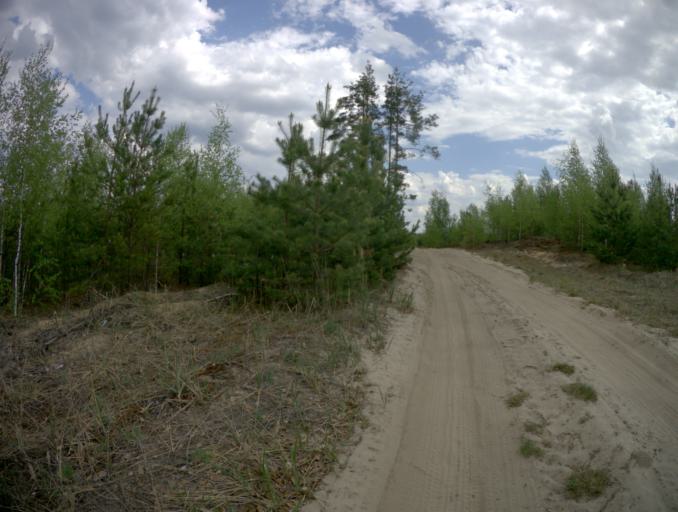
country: RU
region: Ivanovo
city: Talitsy
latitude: 56.4604
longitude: 42.2309
